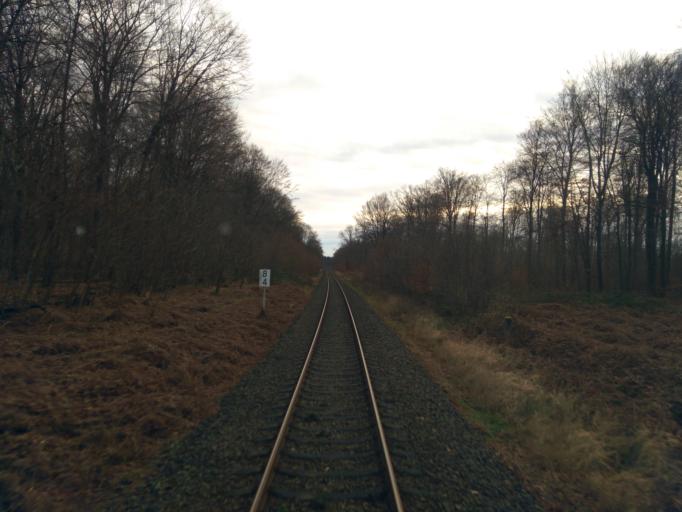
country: DE
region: Lower Saxony
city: Schwienau
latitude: 53.0123
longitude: 10.4616
